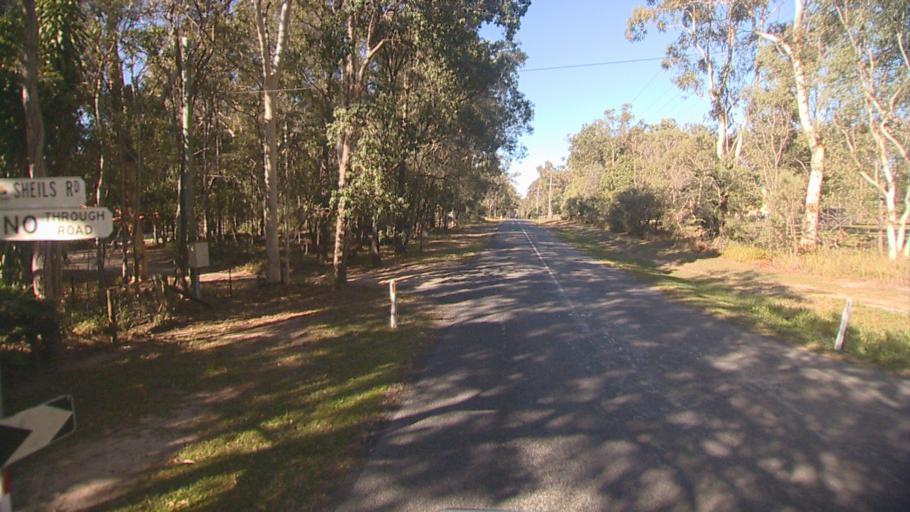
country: AU
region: Queensland
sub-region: Logan
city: Logan Reserve
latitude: -27.7397
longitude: 153.0944
